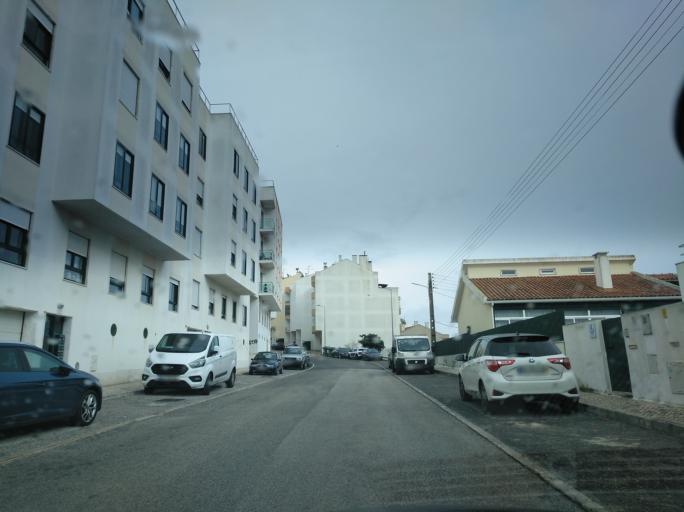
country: PT
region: Lisbon
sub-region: Odivelas
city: Famoes
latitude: 38.7949
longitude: -9.2201
